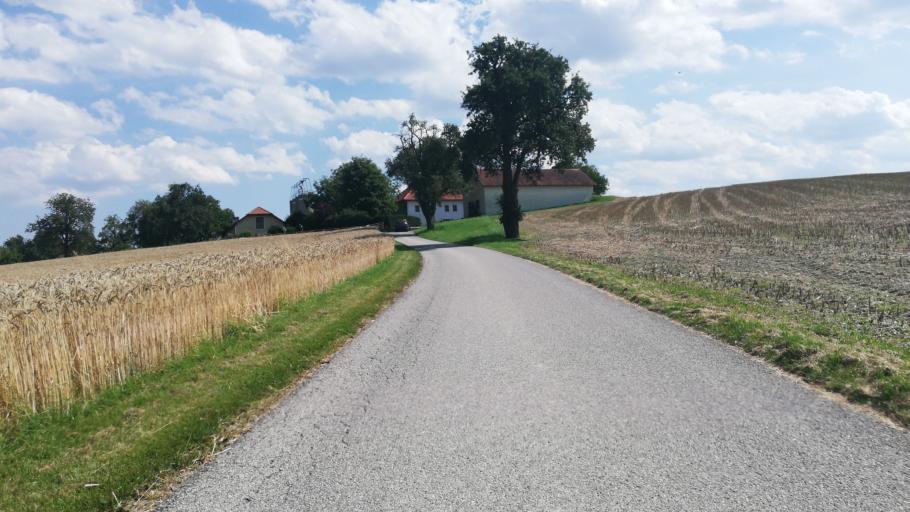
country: AT
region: Upper Austria
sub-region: Wels-Land
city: Pennewang
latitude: 48.1637
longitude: 13.8824
